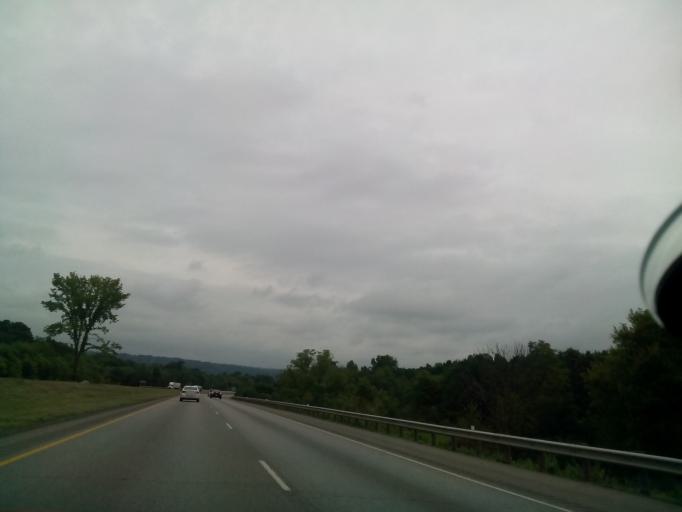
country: US
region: Ohio
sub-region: Trumbull County
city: Masury
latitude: 41.1816
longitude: -80.5261
